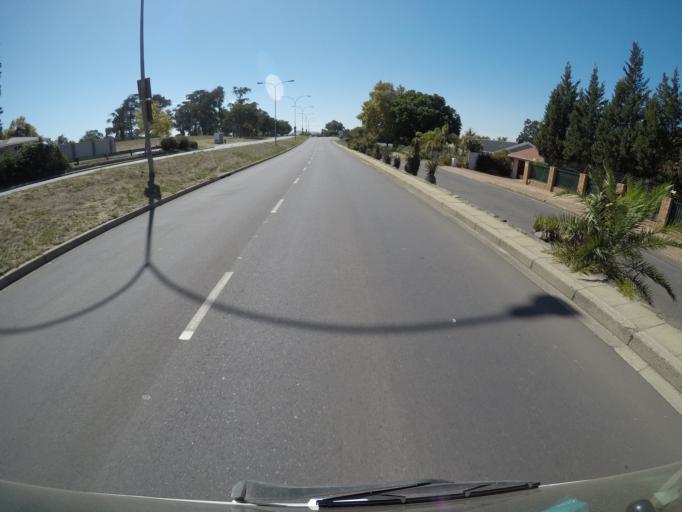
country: ZA
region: Western Cape
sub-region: City of Cape Town
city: Kraaifontein
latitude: -33.8399
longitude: 18.6486
